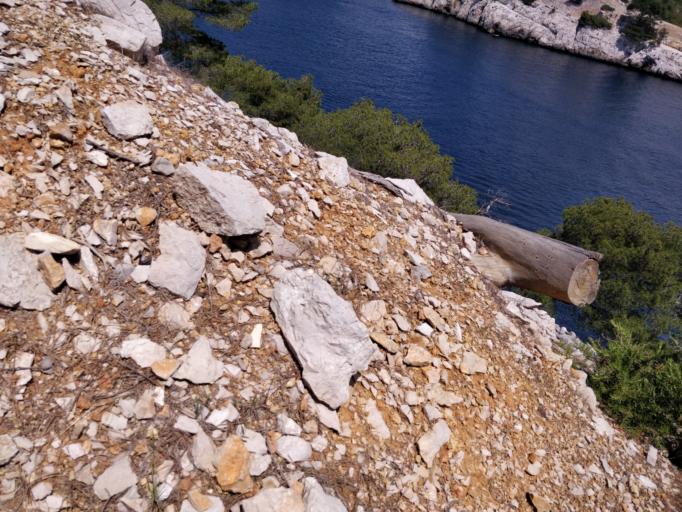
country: FR
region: Provence-Alpes-Cote d'Azur
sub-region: Departement des Bouches-du-Rhone
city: Cassis
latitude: 43.2020
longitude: 5.5114
